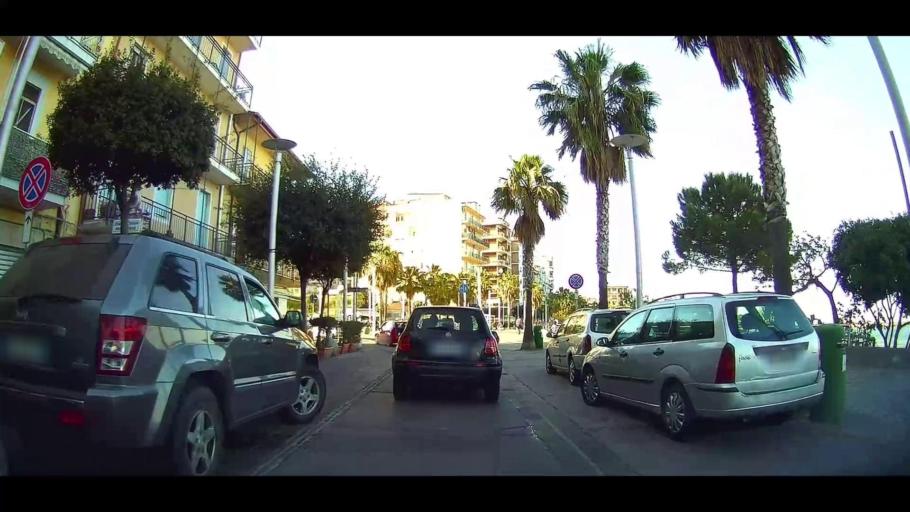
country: IT
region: Calabria
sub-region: Provincia di Crotone
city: Crotone
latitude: 39.0738
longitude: 17.1296
